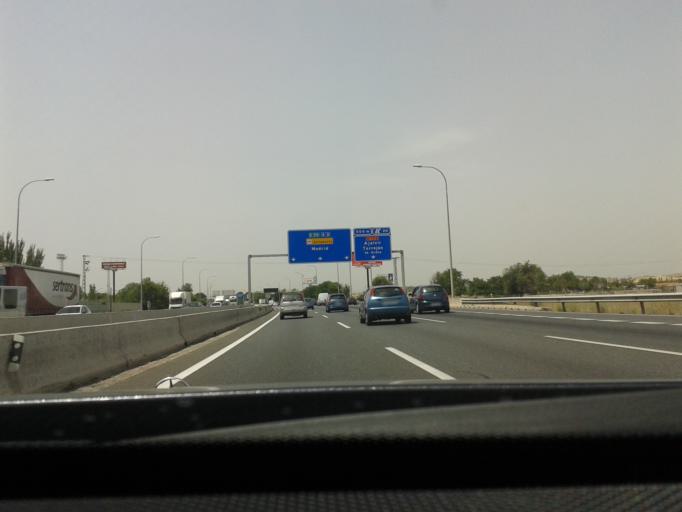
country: ES
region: Madrid
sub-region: Provincia de Madrid
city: Torrejon de Ardoz
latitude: 40.4671
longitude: -3.4689
